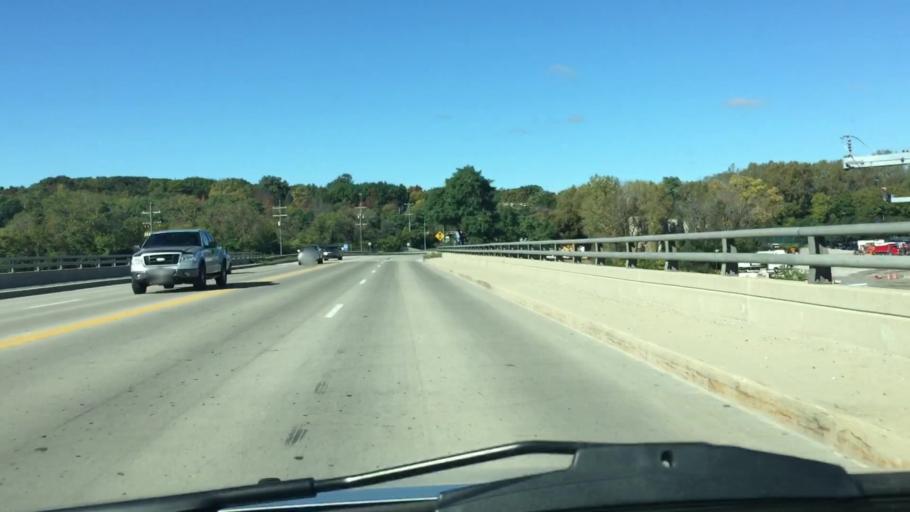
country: US
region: Wisconsin
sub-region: Waukesha County
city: Waukesha
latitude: 43.0382
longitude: -88.2124
